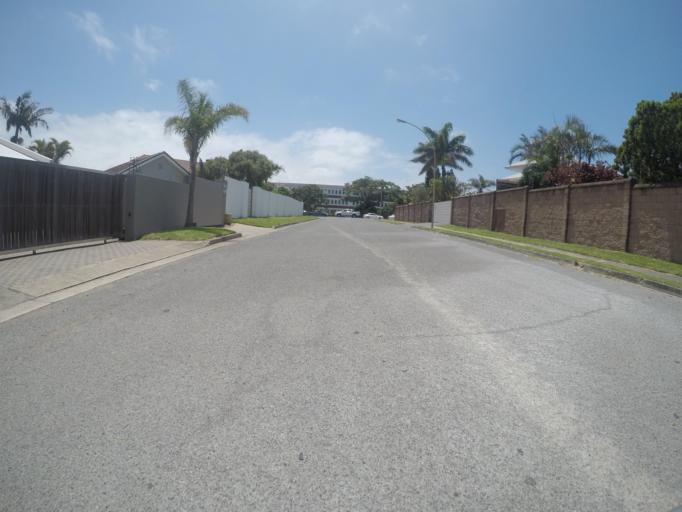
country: ZA
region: Eastern Cape
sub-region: Buffalo City Metropolitan Municipality
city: East London
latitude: -32.9955
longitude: 27.9244
